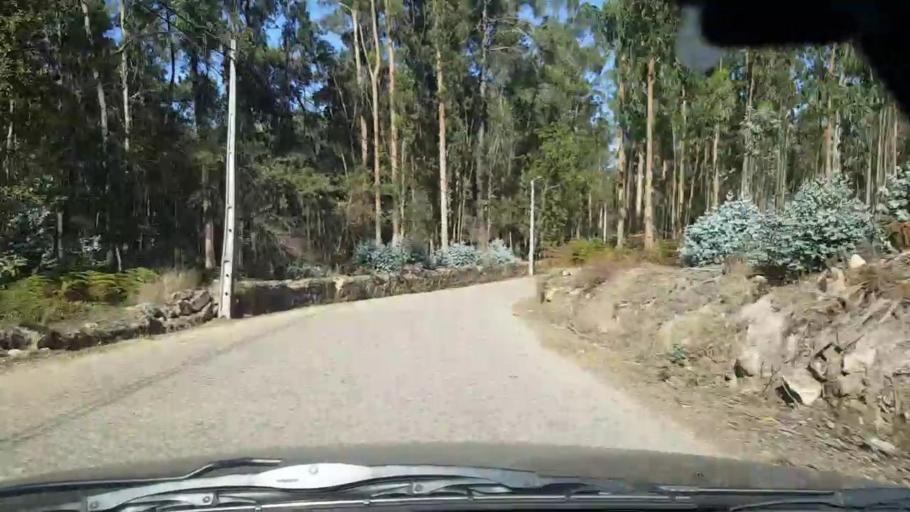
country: PT
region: Braga
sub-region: Vila Nova de Famalicao
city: Ribeirao
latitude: 41.3838
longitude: -8.6400
